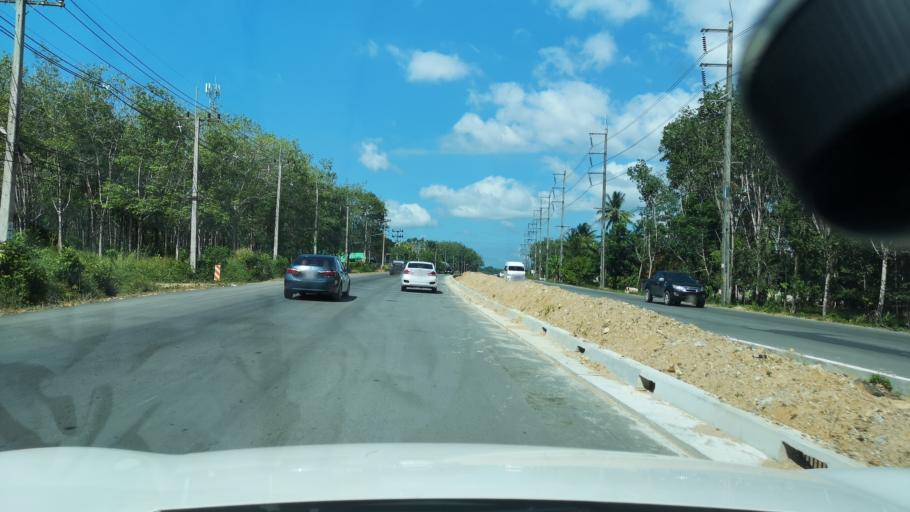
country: TH
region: Phangnga
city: Thai Mueang
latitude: 8.4359
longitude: 98.2571
